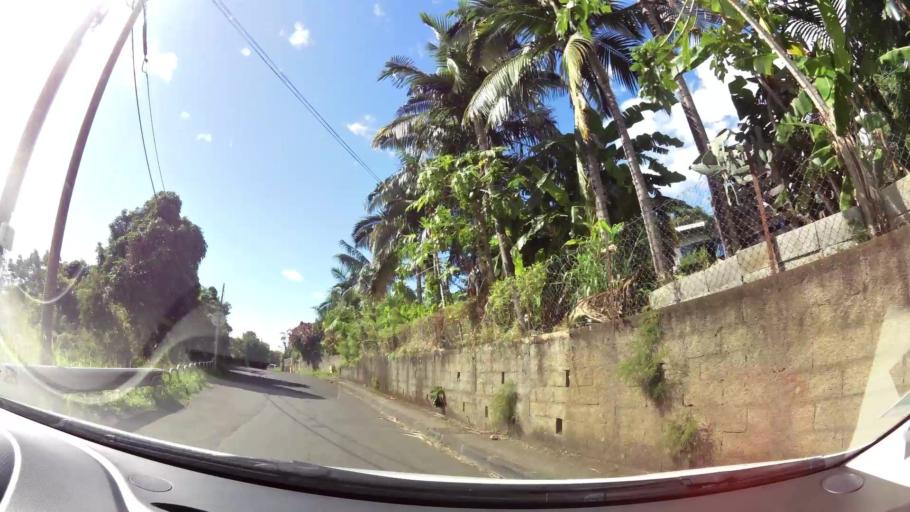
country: RE
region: Reunion
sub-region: Reunion
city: Sainte-Marie
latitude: -20.9188
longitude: 55.4971
